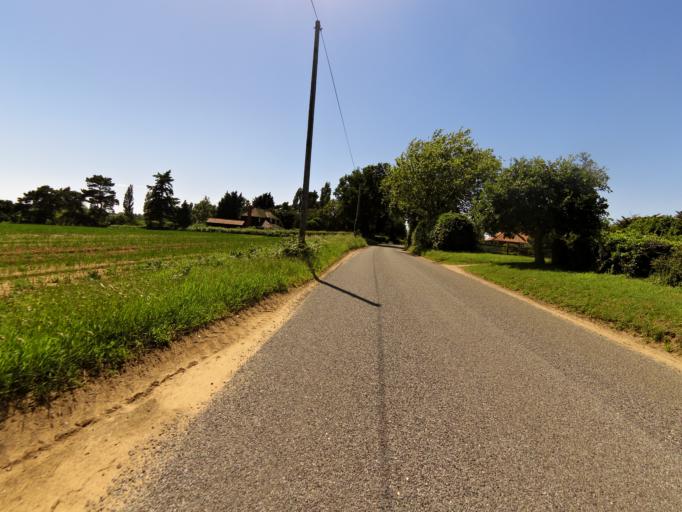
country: GB
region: England
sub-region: Suffolk
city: Felixstowe
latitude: 52.0428
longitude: 1.4200
